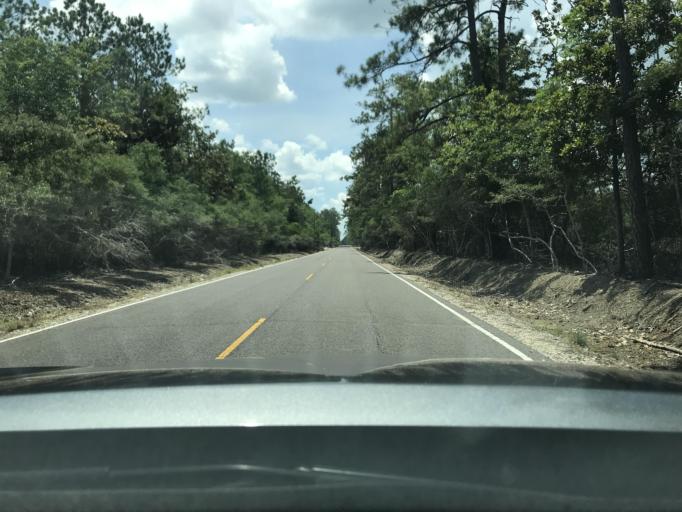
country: US
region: Louisiana
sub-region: Calcasieu Parish
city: Moss Bluff
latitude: 30.3299
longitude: -93.1437
